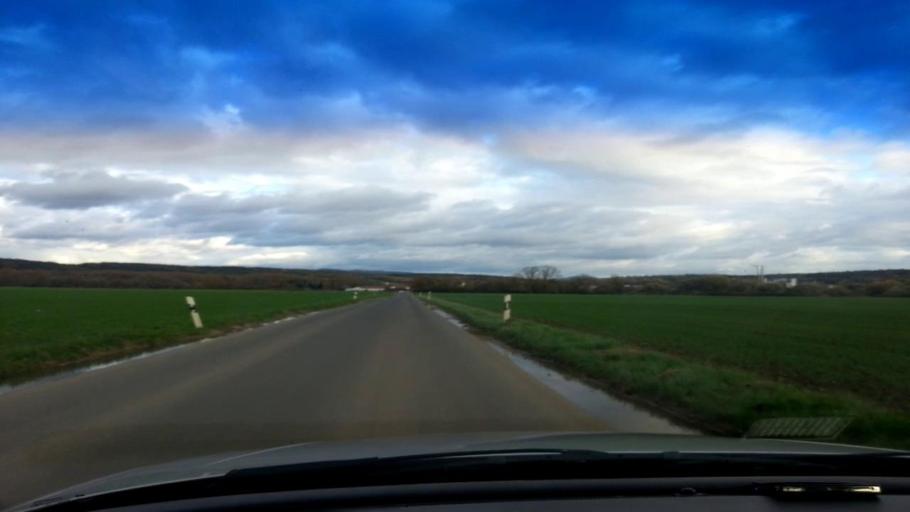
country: DE
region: Bavaria
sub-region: Upper Franconia
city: Zapfendorf
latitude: 50.0233
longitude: 10.9177
